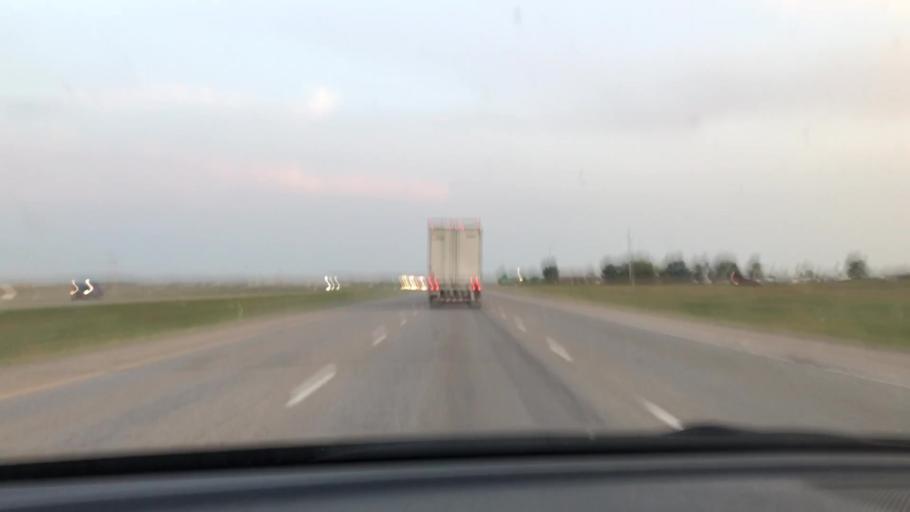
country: CA
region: Alberta
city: Airdrie
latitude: 51.2288
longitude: -114.0018
